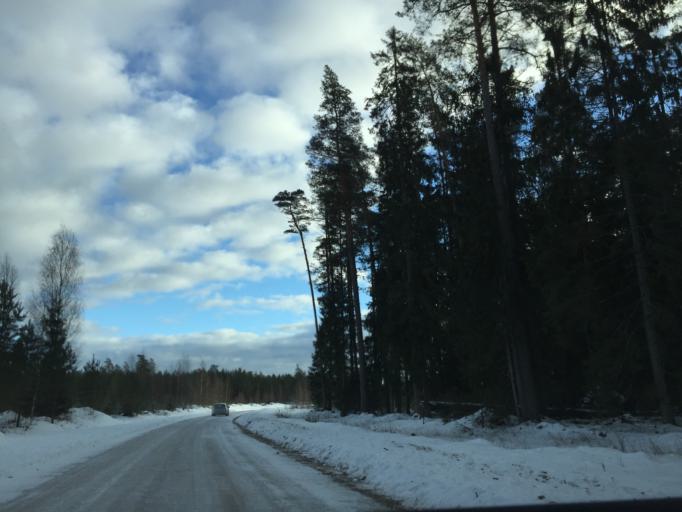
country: LV
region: Lielvarde
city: Lielvarde
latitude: 56.5661
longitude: 24.8301
